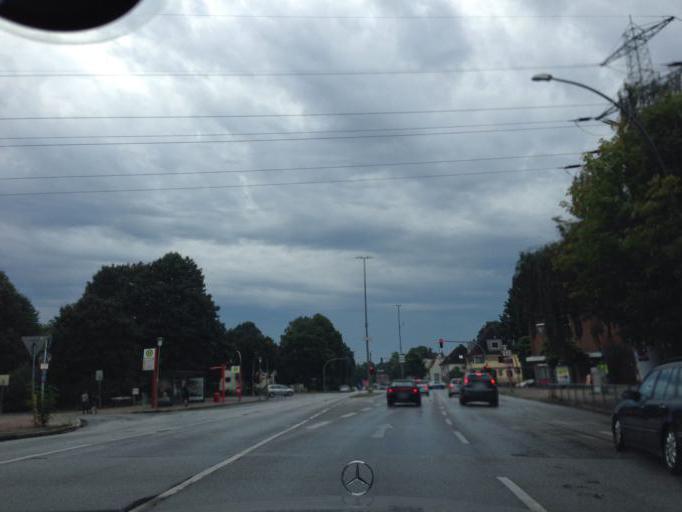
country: DE
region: Hamburg
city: Steilshoop
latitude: 53.6095
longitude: 10.0732
